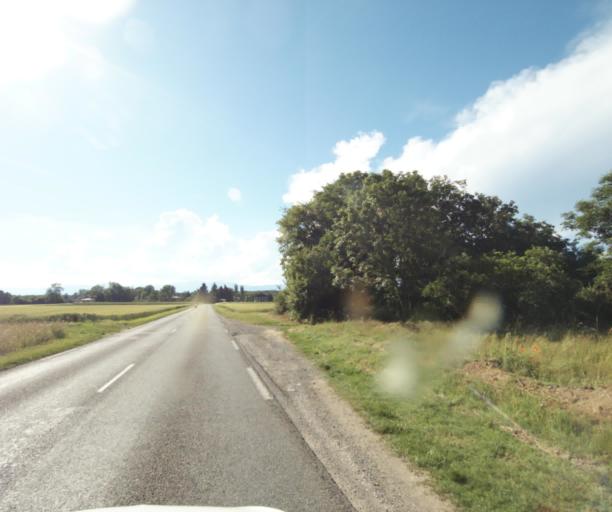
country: FR
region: Rhone-Alpes
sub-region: Departement de la Haute-Savoie
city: Sciez
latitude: 46.3352
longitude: 6.3652
